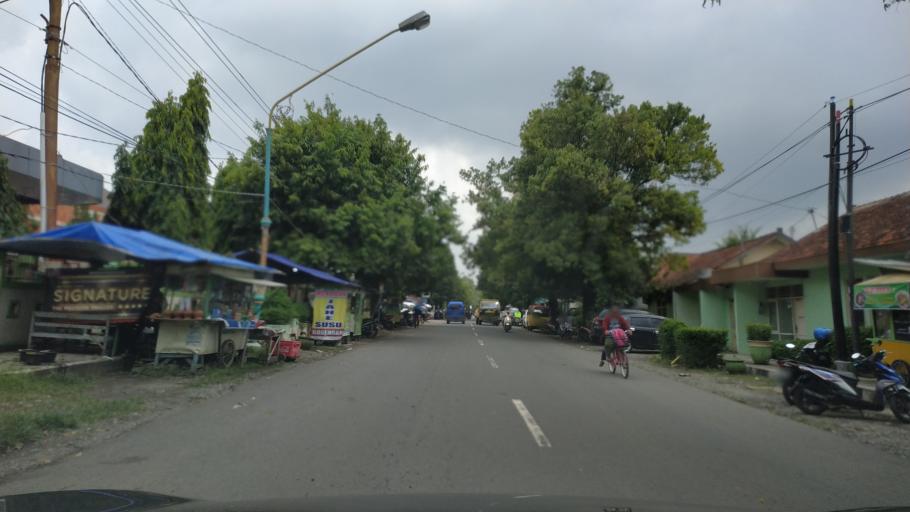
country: ID
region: Central Java
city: Slawi
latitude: -6.9930
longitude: 109.1383
